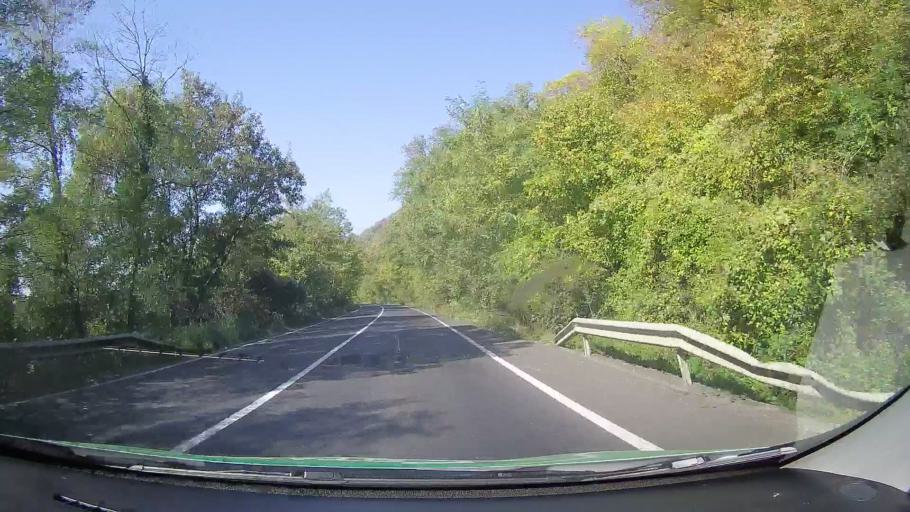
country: RO
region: Arad
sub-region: Comuna Savarsin
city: Savarsin
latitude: 46.0115
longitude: 22.2684
